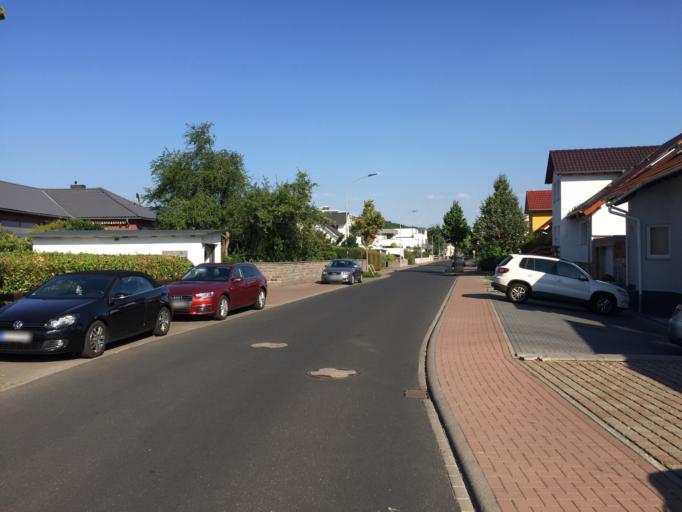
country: DE
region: Hesse
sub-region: Regierungsbezirk Giessen
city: Langgons
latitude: 50.5404
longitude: 8.6691
